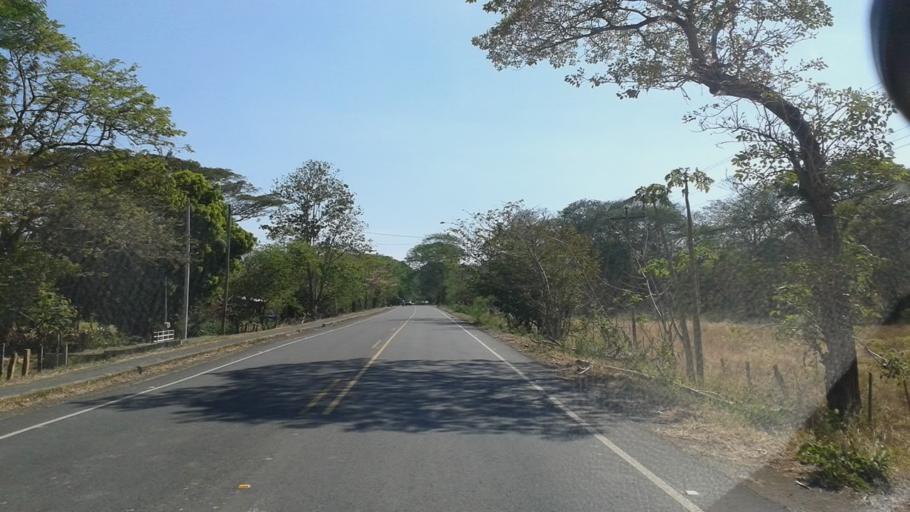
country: CR
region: Guanacaste
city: Santa Cruz
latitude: 10.2423
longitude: -85.7206
